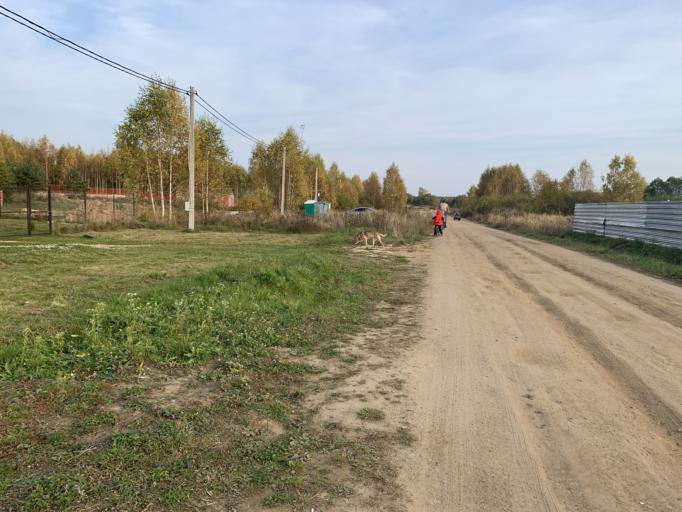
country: RU
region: Jaroslavl
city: Petrovsk
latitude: 56.9808
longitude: 39.3751
